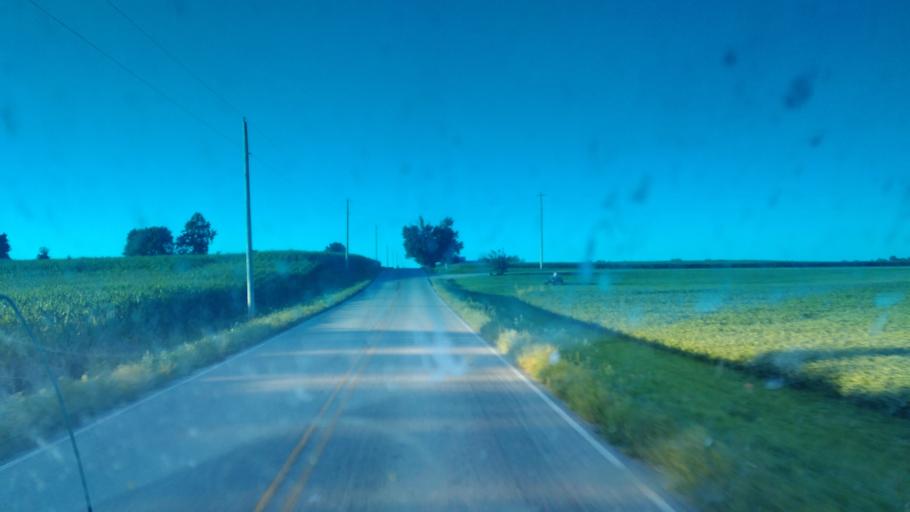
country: US
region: Ohio
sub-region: Wyandot County
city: Upper Sandusky
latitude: 40.8825
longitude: -83.1700
